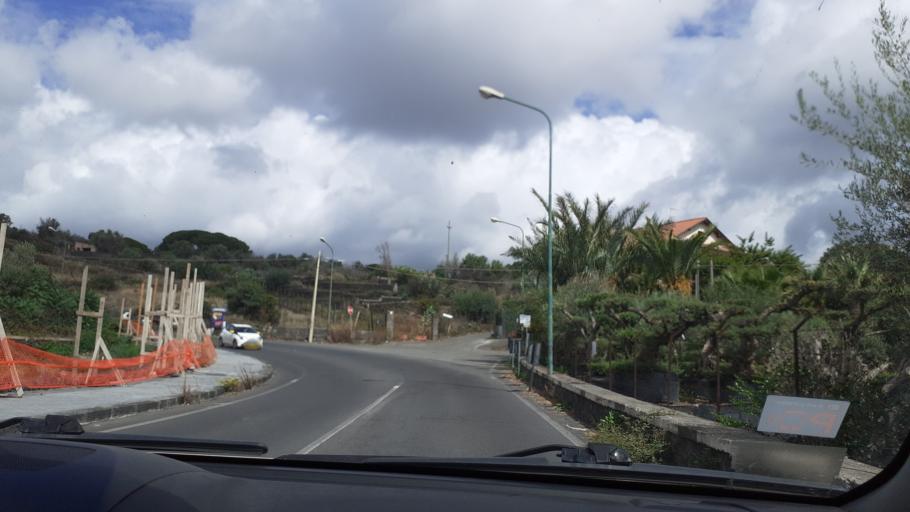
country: IT
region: Sicily
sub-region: Catania
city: Carrubazza-Motta
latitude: 37.5574
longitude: 15.1087
